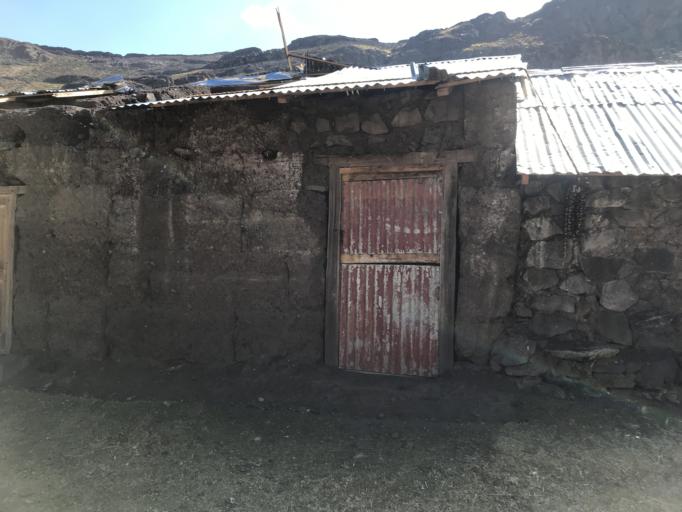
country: PE
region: Lima
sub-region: Provincia de Yauyos
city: Tupe
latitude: -12.6394
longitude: -75.7254
